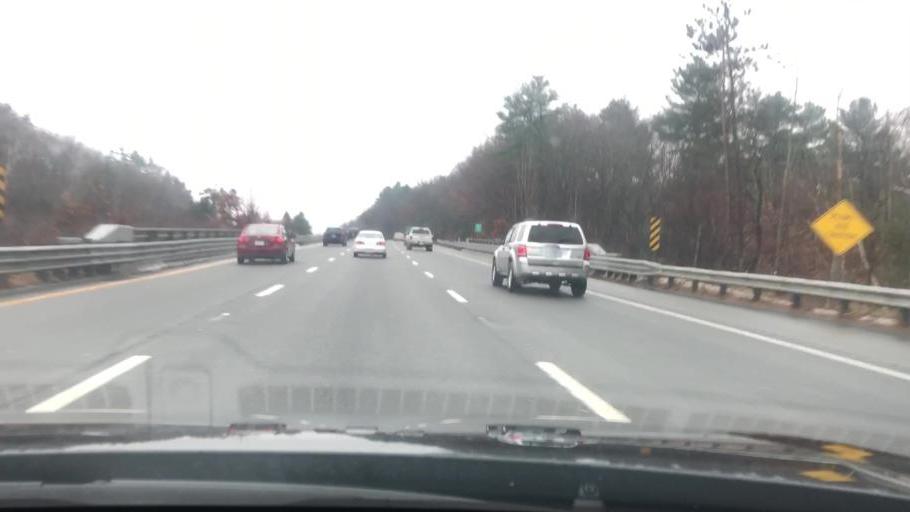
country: US
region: Massachusetts
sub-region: Middlesex County
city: Westford
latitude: 42.5779
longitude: -71.4117
